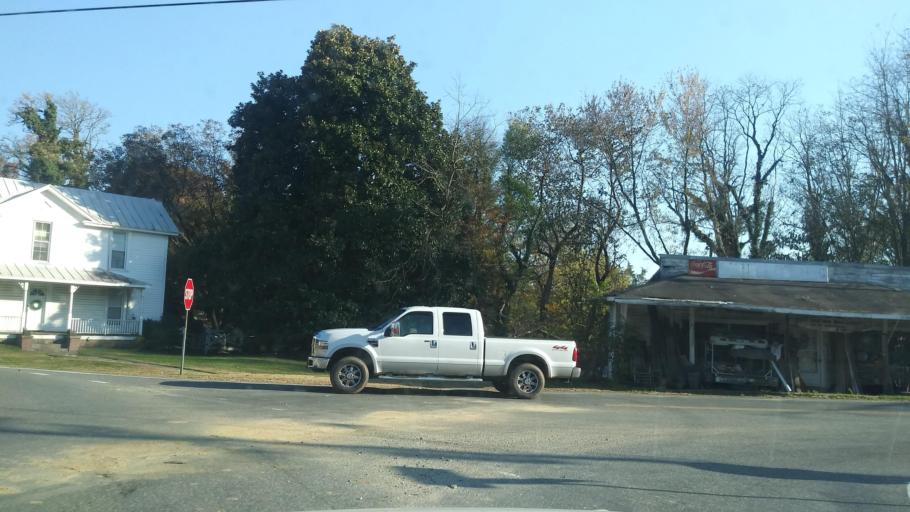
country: US
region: North Carolina
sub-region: Guilford County
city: McLeansville
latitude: 36.2128
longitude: -79.7134
